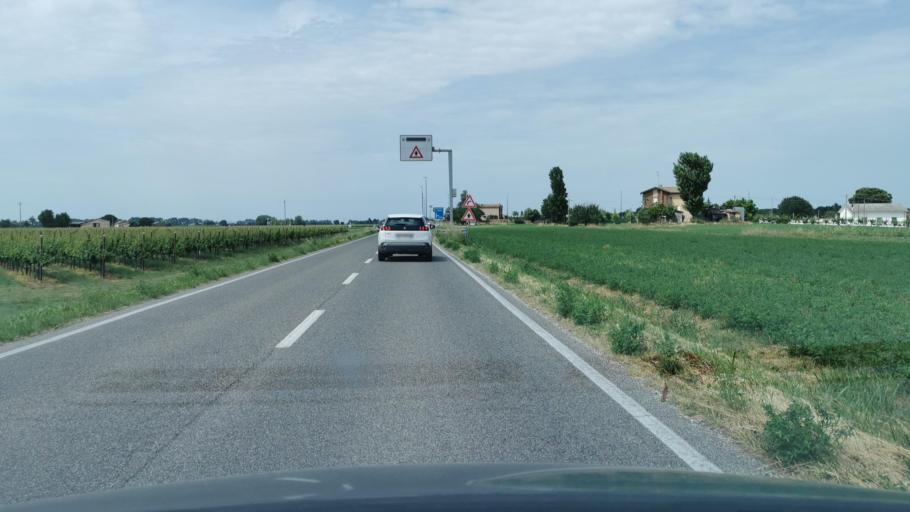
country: IT
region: Emilia-Romagna
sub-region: Provincia di Ravenna
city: Savarna-Conventella
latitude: 44.5073
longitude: 12.1004
